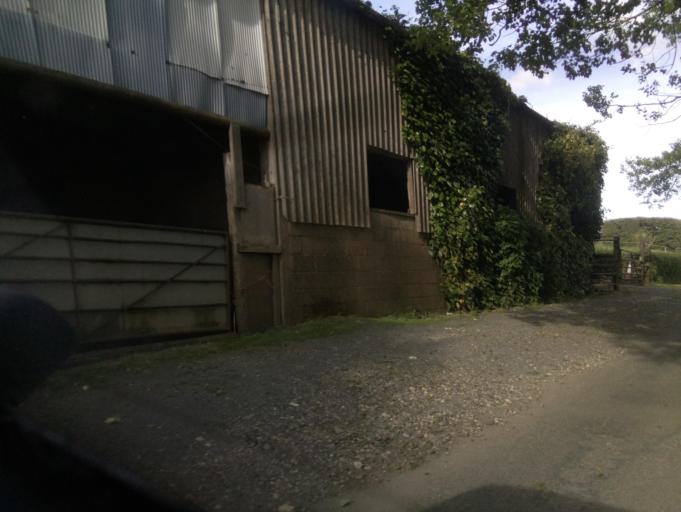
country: GB
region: England
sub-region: Gloucestershire
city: Shipton Village
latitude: 51.8787
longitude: -1.9440
